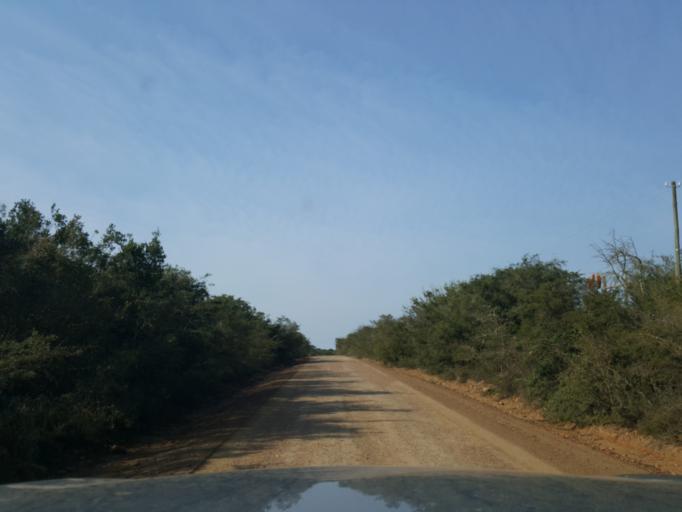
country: ZA
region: Eastern Cape
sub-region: Cacadu District Municipality
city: Grahamstown
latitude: -33.4029
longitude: 26.2934
